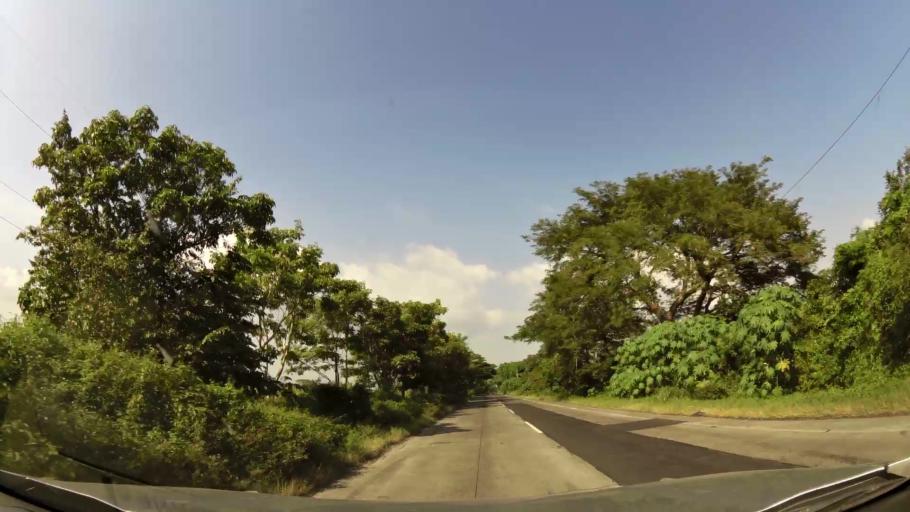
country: GT
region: Escuintla
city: Puerto San Jose
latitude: 13.9942
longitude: -90.7880
